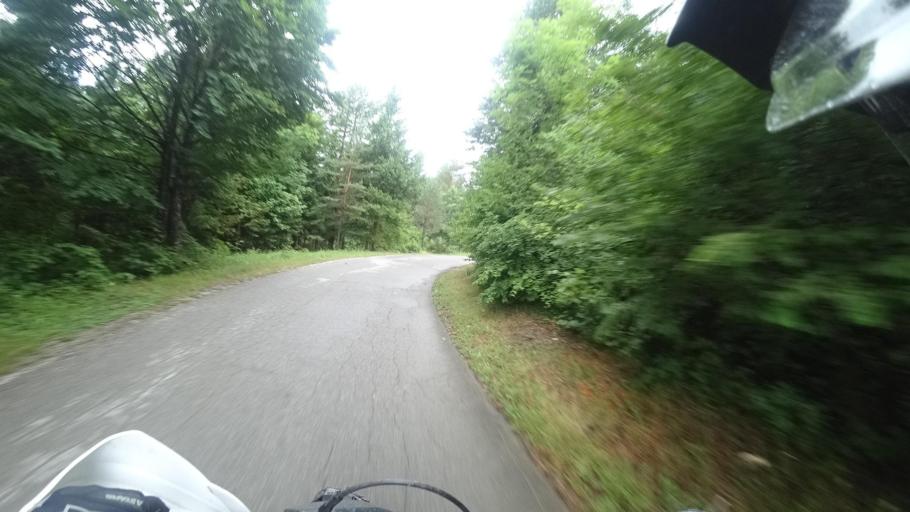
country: HR
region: Karlovacka
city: Plaski
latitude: 45.0016
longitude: 15.4202
